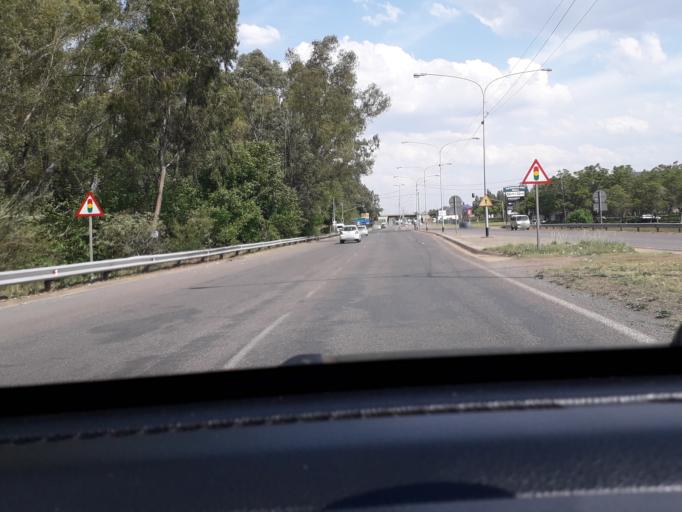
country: ZA
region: Gauteng
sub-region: City of Tshwane Metropolitan Municipality
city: Centurion
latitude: -25.8542
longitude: 28.2182
